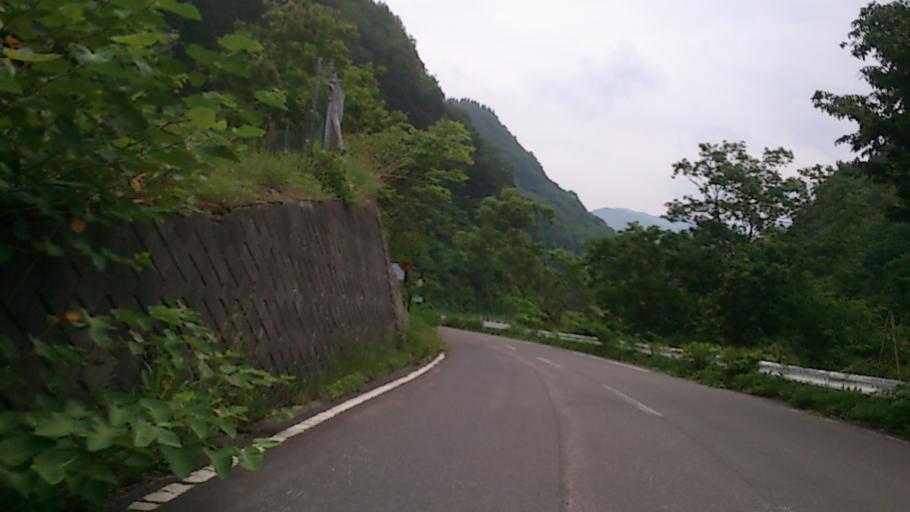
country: JP
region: Aomori
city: Hirosaki
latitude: 40.5636
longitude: 140.2835
